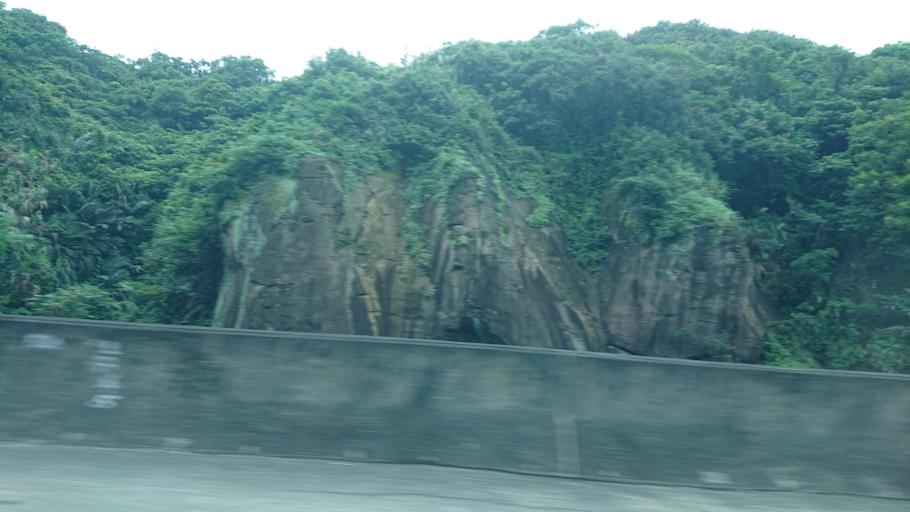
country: TW
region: Taiwan
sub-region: Keelung
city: Keelung
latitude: 25.1210
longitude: 121.8183
